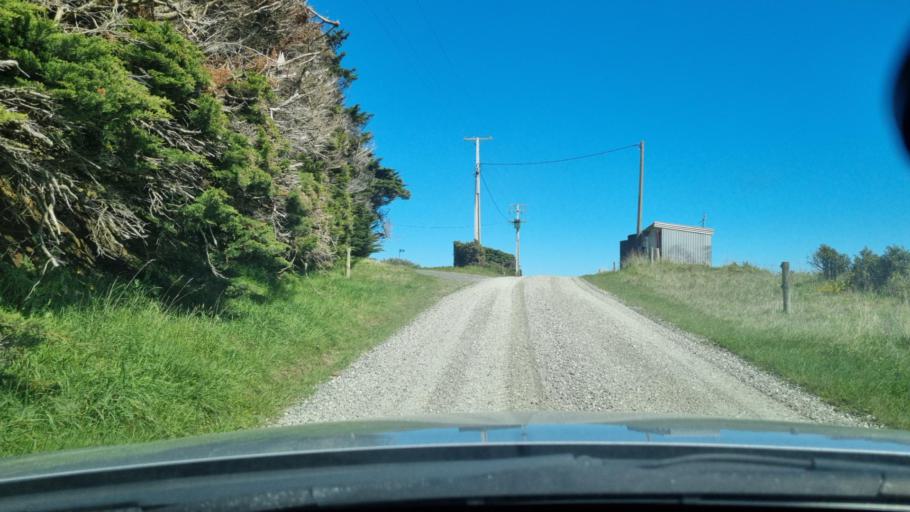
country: NZ
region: Southland
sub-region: Invercargill City
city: Invercargill
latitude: -46.3936
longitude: 168.2582
